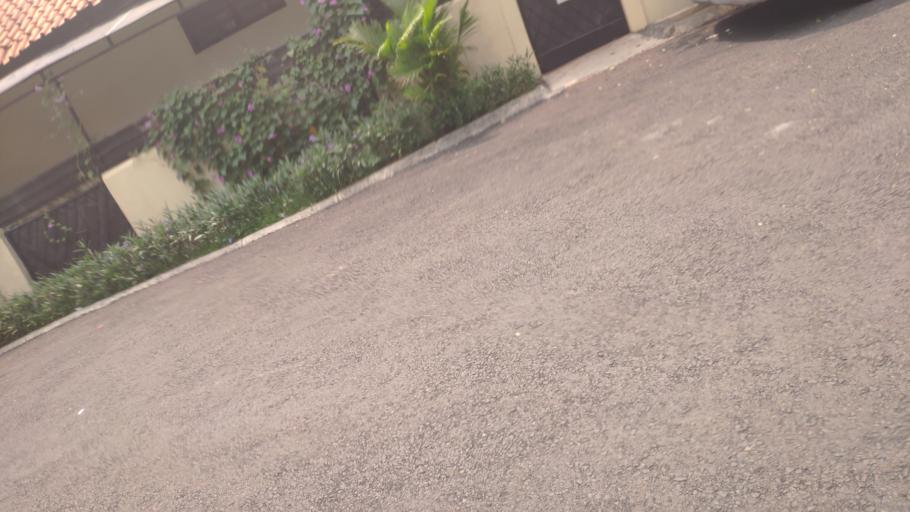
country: ID
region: Jakarta Raya
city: Jakarta
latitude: -6.2639
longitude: 106.8288
